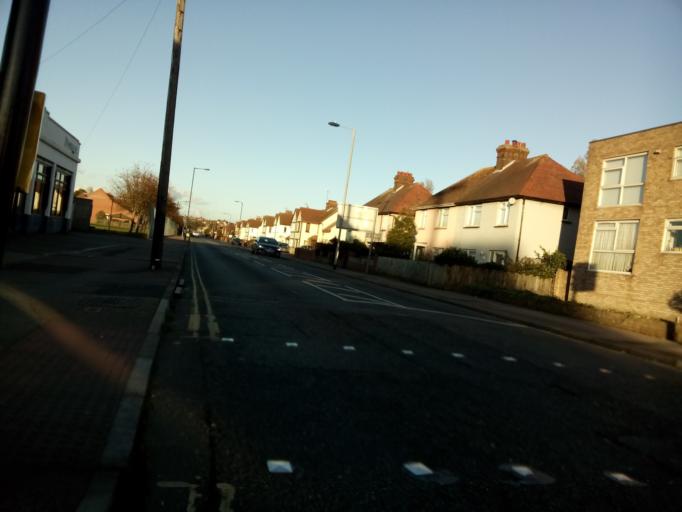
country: GB
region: England
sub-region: Suffolk
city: Felixstowe
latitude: 51.9524
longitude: 1.3359
